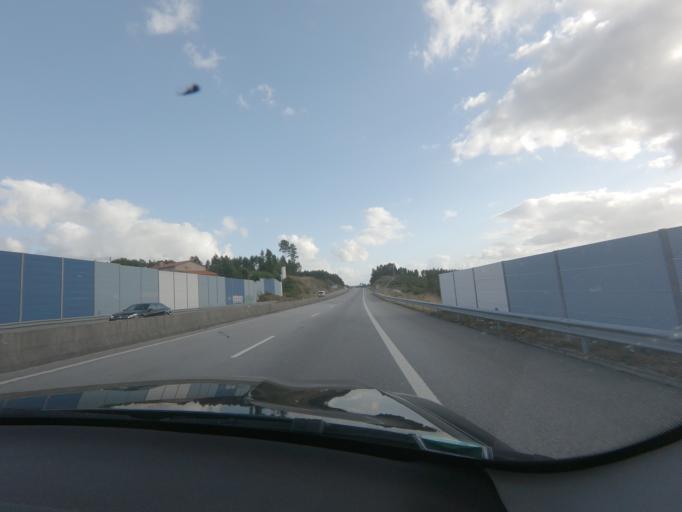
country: PT
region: Viseu
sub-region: Viseu
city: Viseu
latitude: 40.6349
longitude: -7.9581
